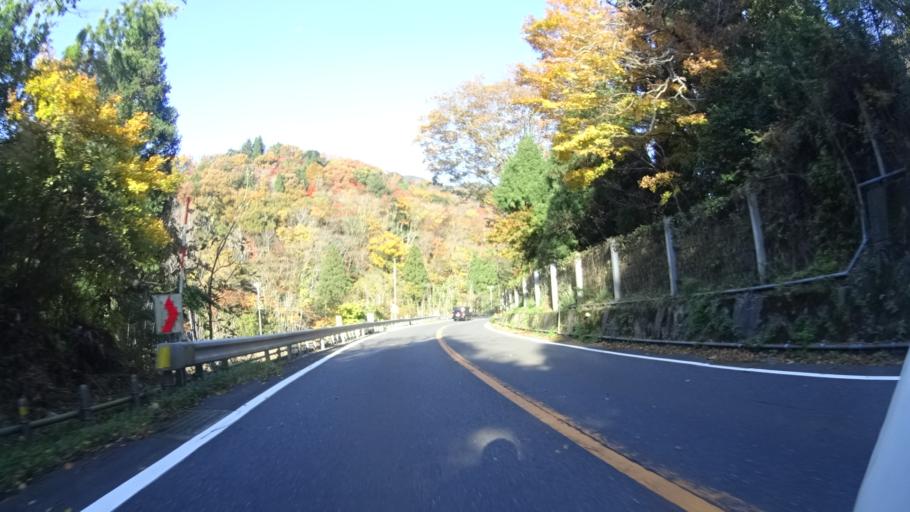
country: JP
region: Fukui
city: Tsuruga
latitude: 35.5478
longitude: 136.0986
